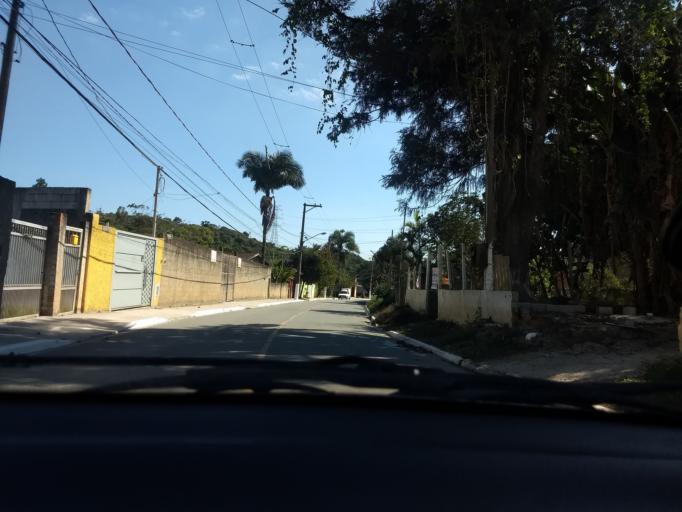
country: BR
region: Sao Paulo
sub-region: Embu-Guacu
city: Embu Guacu
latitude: -23.8110
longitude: -46.7591
